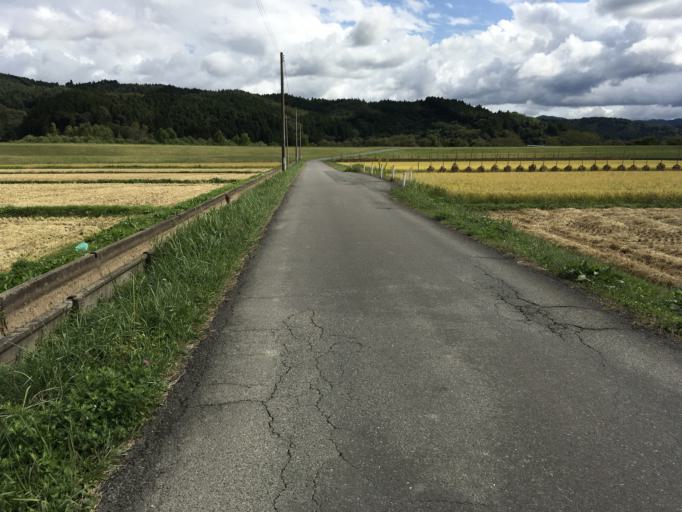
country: JP
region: Miyagi
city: Wakuya
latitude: 38.7284
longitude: 141.2905
